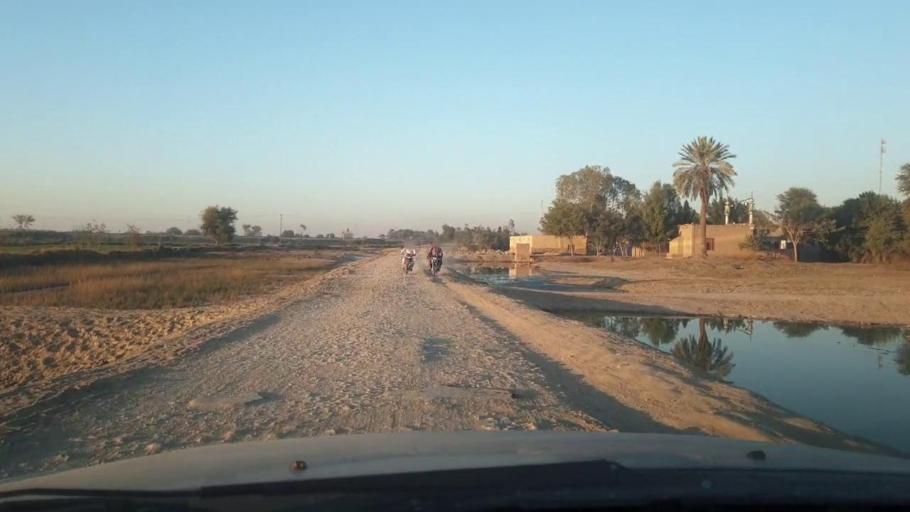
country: PK
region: Sindh
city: Pano Aqil
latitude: 27.9153
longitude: 69.1939
